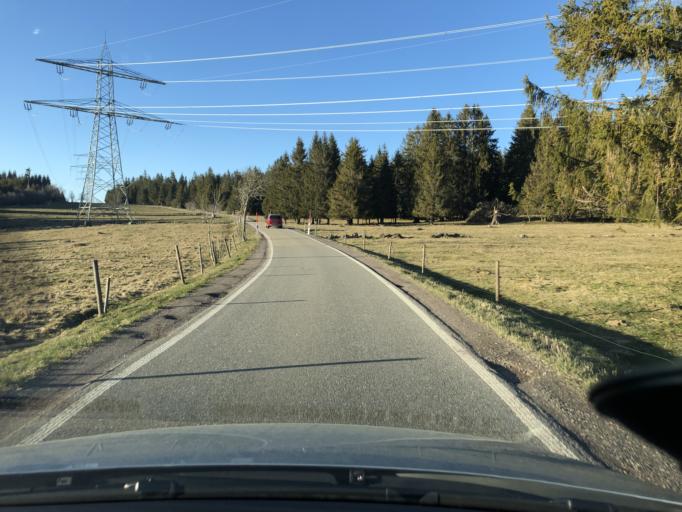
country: DE
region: Baden-Wuerttemberg
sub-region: Freiburg Region
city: Schluchsee
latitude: 47.8116
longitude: 8.2143
